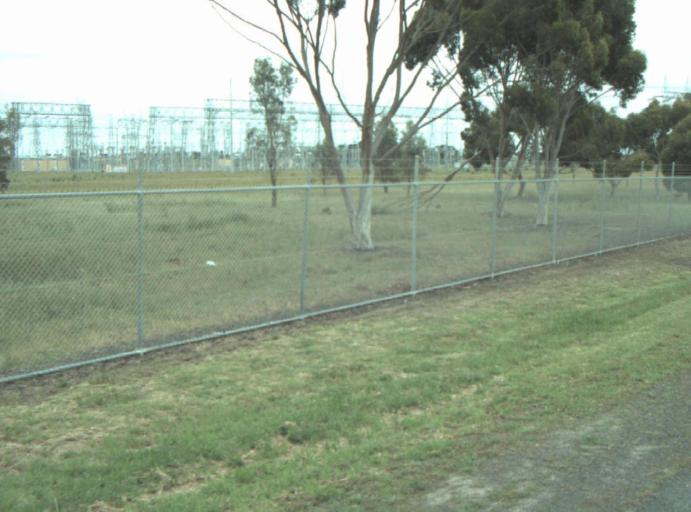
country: AU
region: Victoria
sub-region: Greater Geelong
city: Bell Post Hill
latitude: -38.0372
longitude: 144.3021
